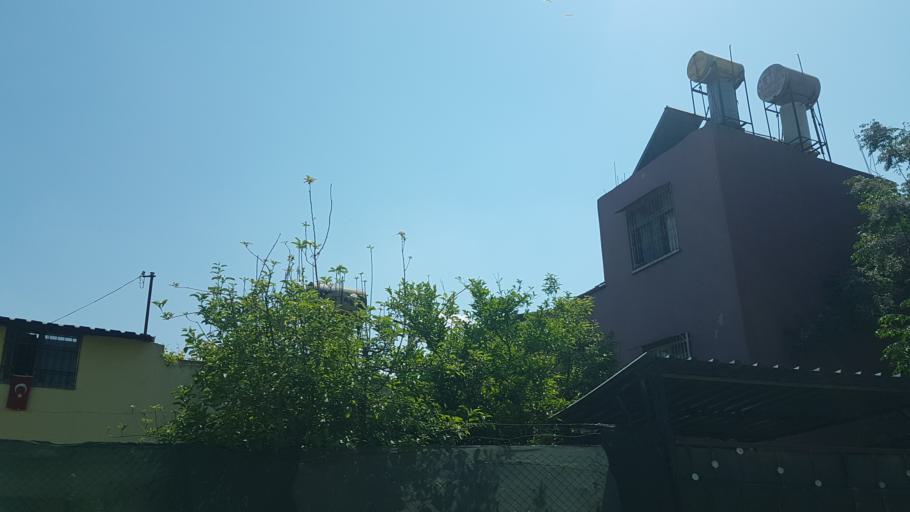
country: TR
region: Adana
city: Adana
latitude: 37.0236
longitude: 35.3683
